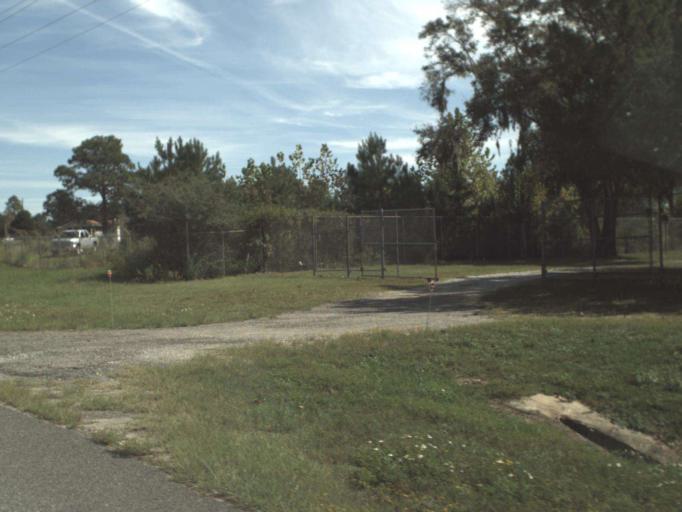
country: US
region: Florida
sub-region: Washington County
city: Chipley
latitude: 30.5697
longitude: -85.6032
